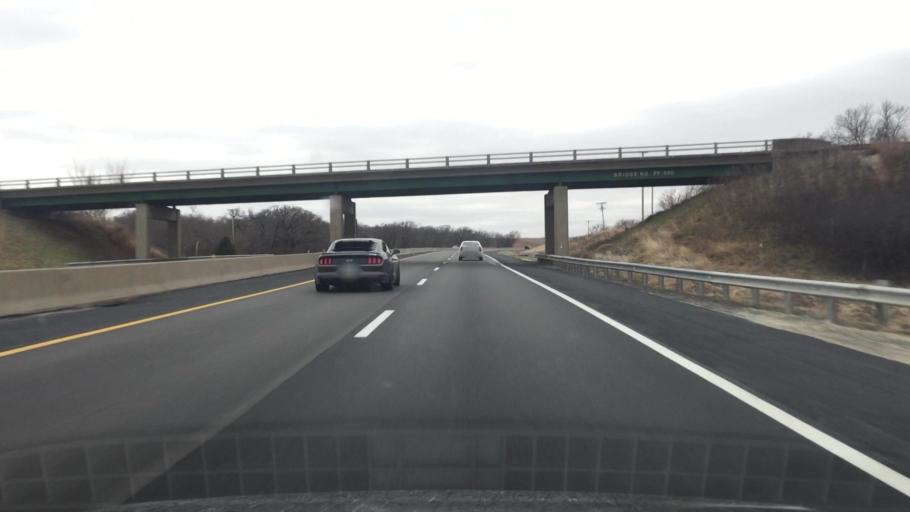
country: US
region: Kansas
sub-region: Chase County
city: Cottonwood Falls
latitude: 38.1244
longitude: -96.5535
